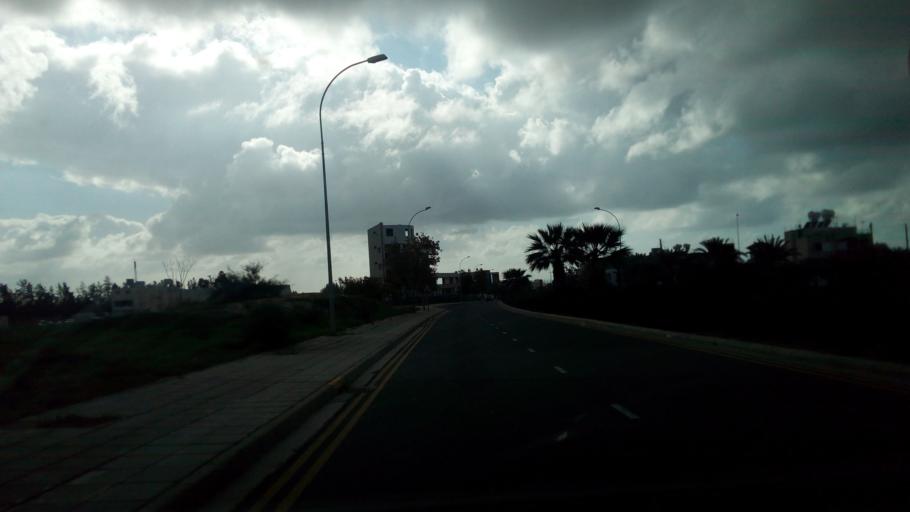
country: CY
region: Pafos
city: Paphos
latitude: 34.7799
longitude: 32.4446
